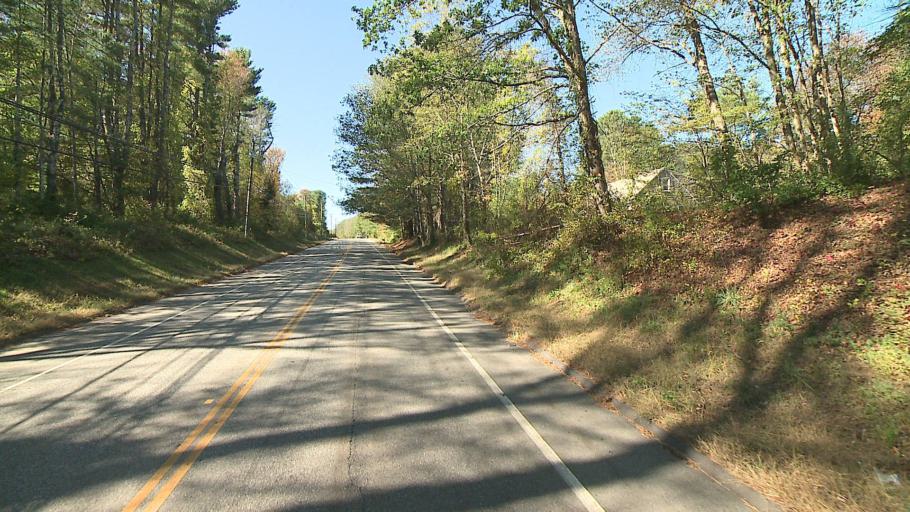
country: US
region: Connecticut
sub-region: Tolland County
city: Hebron
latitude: 41.6580
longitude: -72.3748
